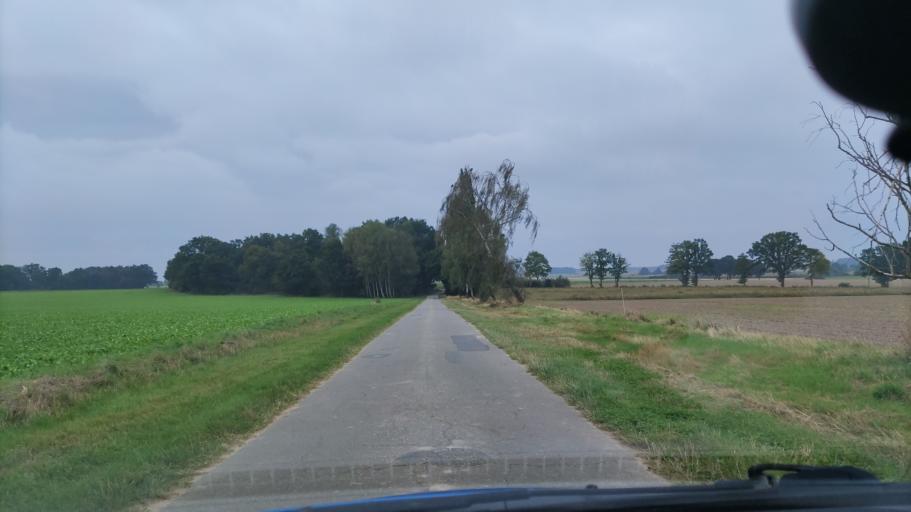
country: DE
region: Lower Saxony
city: Altenmedingen
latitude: 53.1285
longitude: 10.6213
